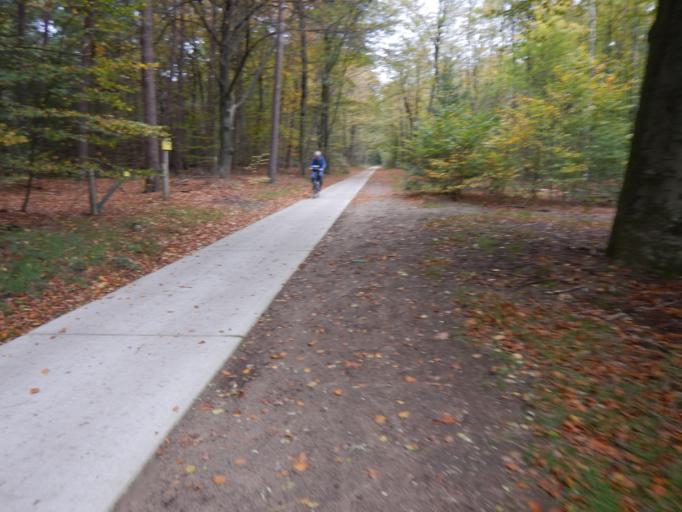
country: NL
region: Gelderland
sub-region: Gemeente Ermelo
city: Ermelo
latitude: 52.2777
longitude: 5.6290
